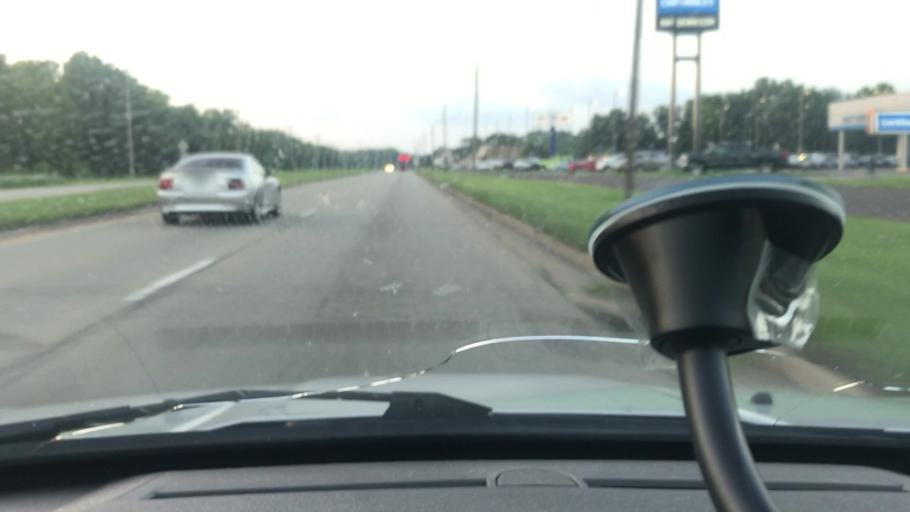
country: US
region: Illinois
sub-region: Tazewell County
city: North Pekin
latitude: 40.5998
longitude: -89.6385
